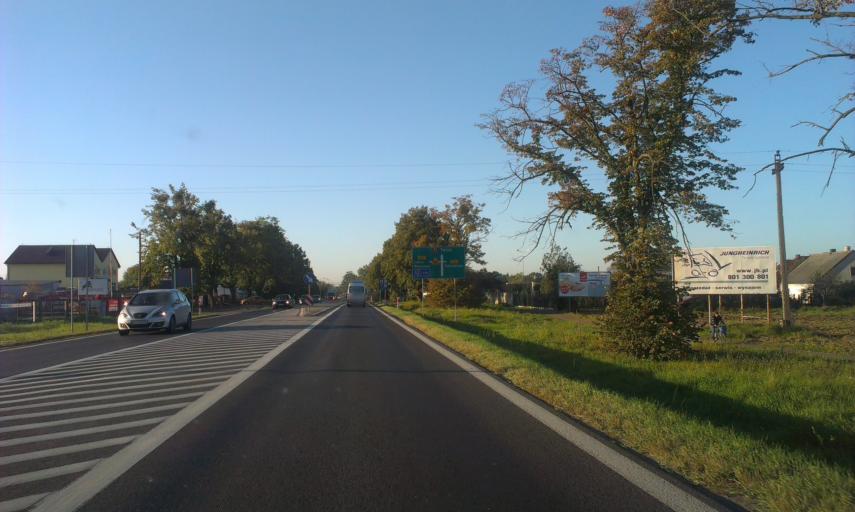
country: PL
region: Kujawsko-Pomorskie
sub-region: Powiat torunski
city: Lysomice
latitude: 53.0905
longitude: 18.6206
